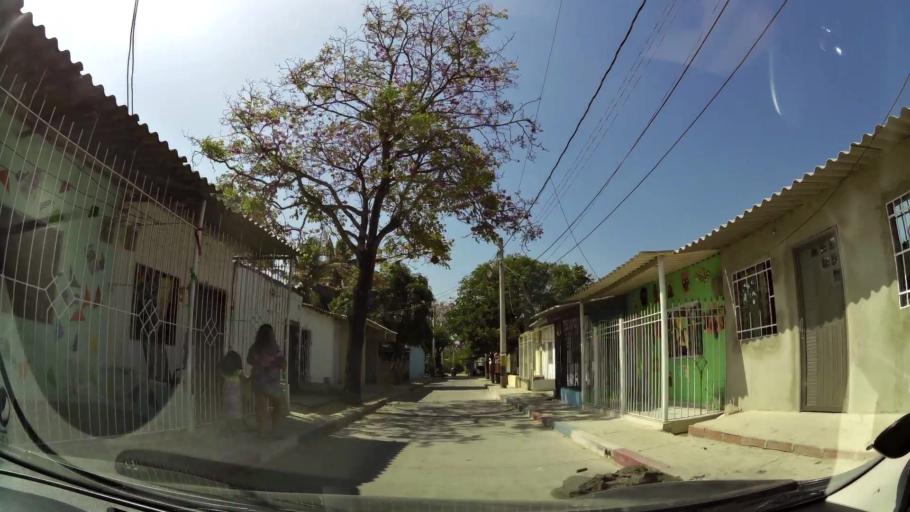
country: CO
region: Atlantico
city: Barranquilla
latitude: 10.9643
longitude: -74.8303
